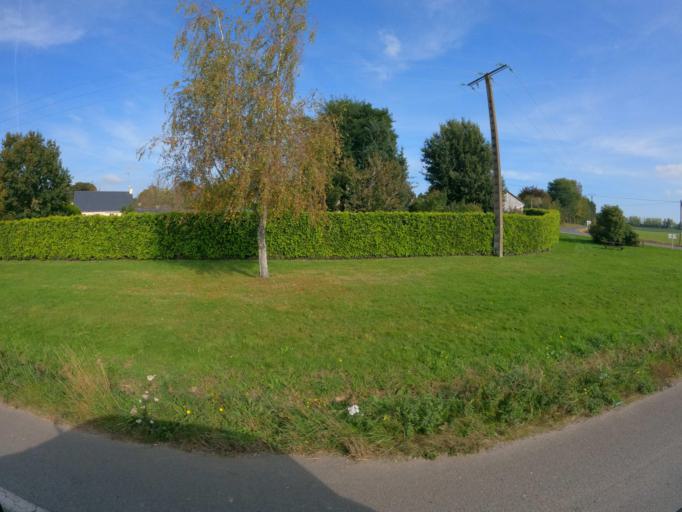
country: FR
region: Brittany
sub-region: Departement du Morbihan
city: Guillac
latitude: 47.8611
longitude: -2.4245
